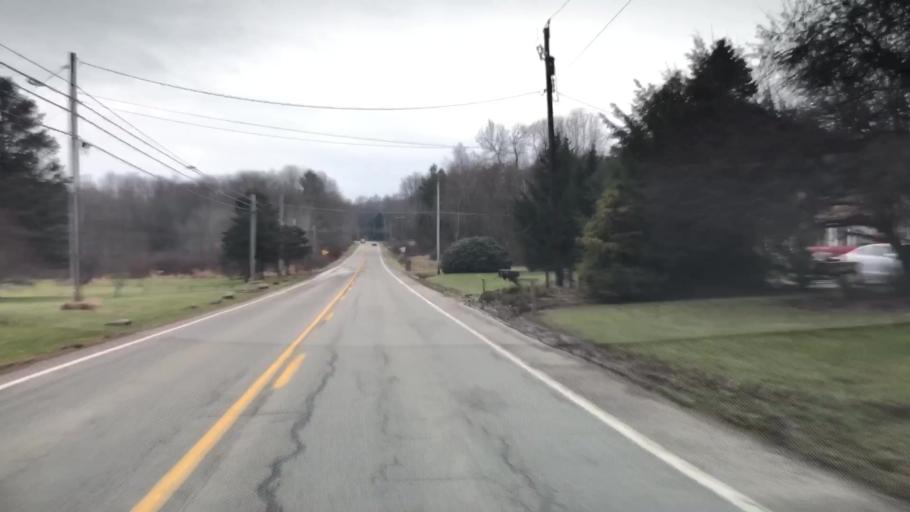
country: US
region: Pennsylvania
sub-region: Mercer County
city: Grove City
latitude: 41.1287
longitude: -80.0724
